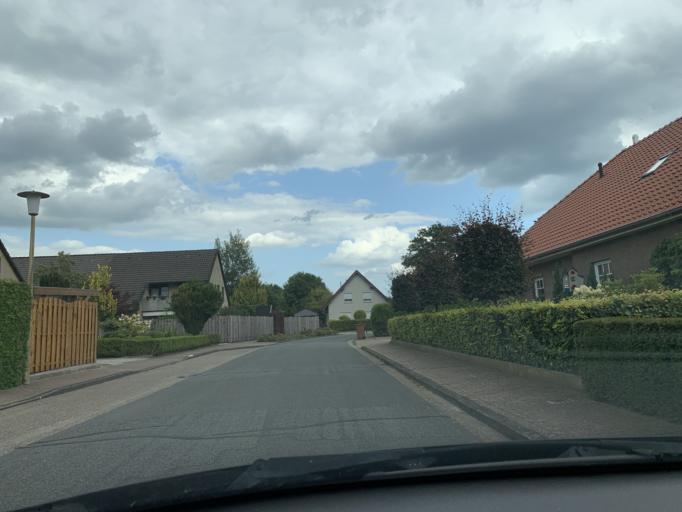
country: DE
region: Lower Saxony
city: Westerstede
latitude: 53.2568
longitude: 7.9403
